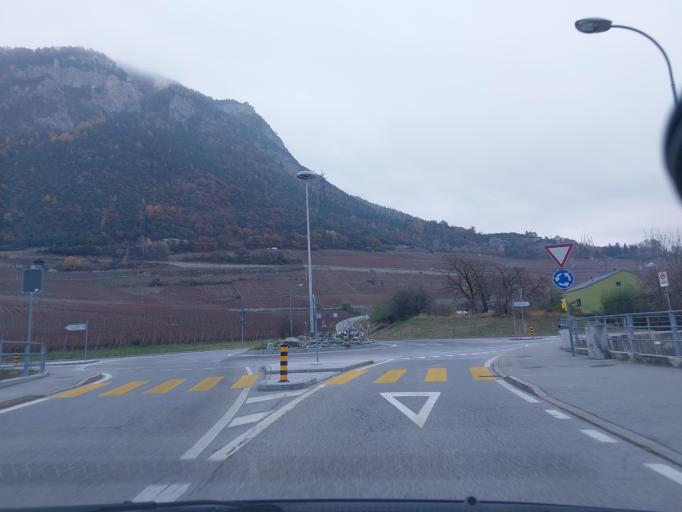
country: CH
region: Valais
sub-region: Sion District
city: Saint-Leonard
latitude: 46.2351
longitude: 7.4084
